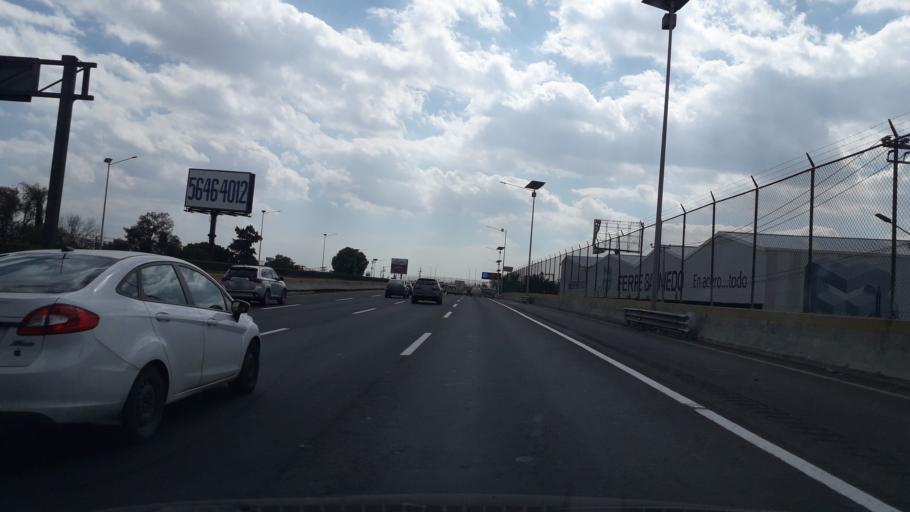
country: MX
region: Mexico
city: Ecatepec
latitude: 19.6001
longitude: -99.0393
